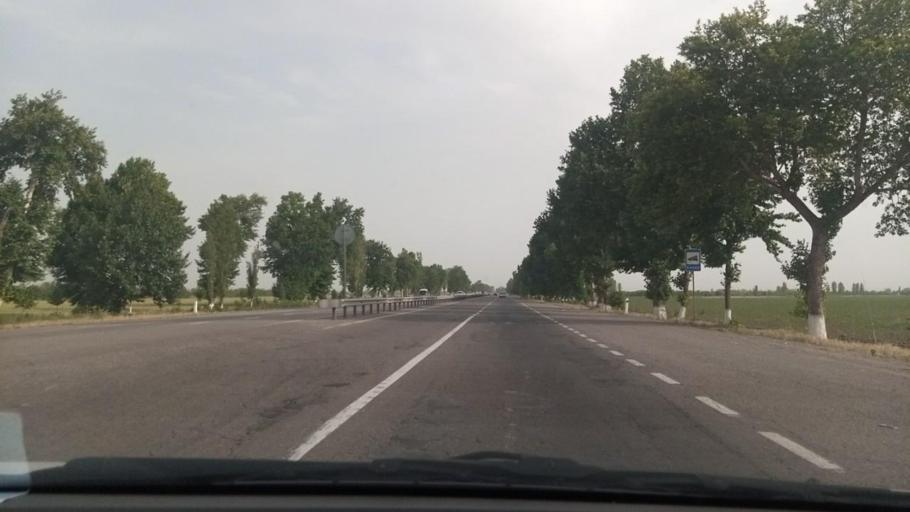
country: UZ
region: Toshkent Shahri
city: Bektemir
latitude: 41.2049
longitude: 69.4028
